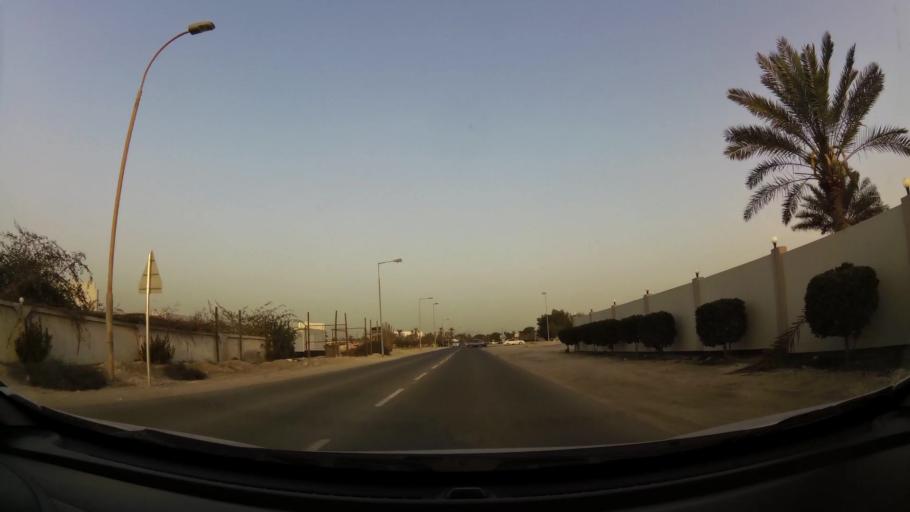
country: BH
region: Manama
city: Jidd Hafs
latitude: 26.1968
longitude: 50.4750
